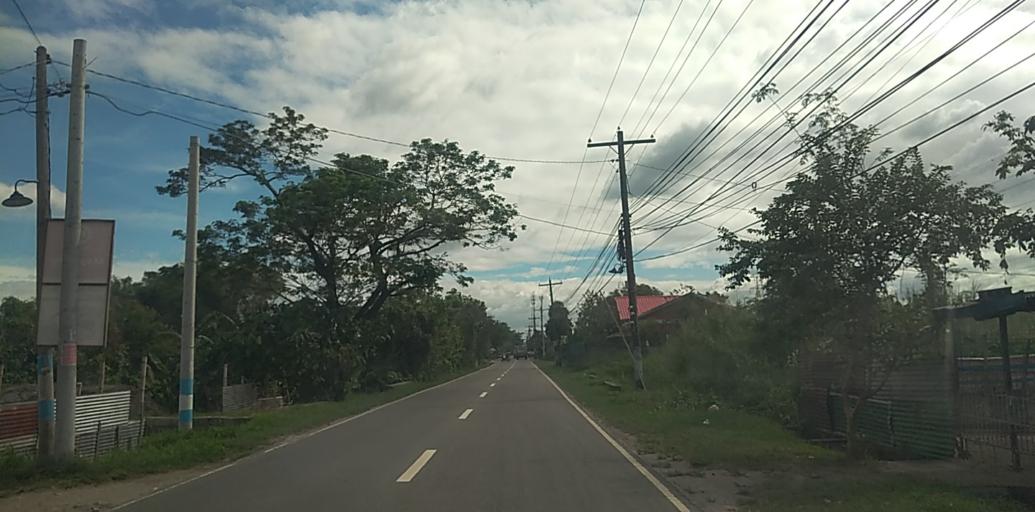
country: PH
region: Central Luzon
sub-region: Province of Pampanga
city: Buensuseso
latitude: 15.1838
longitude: 120.6762
